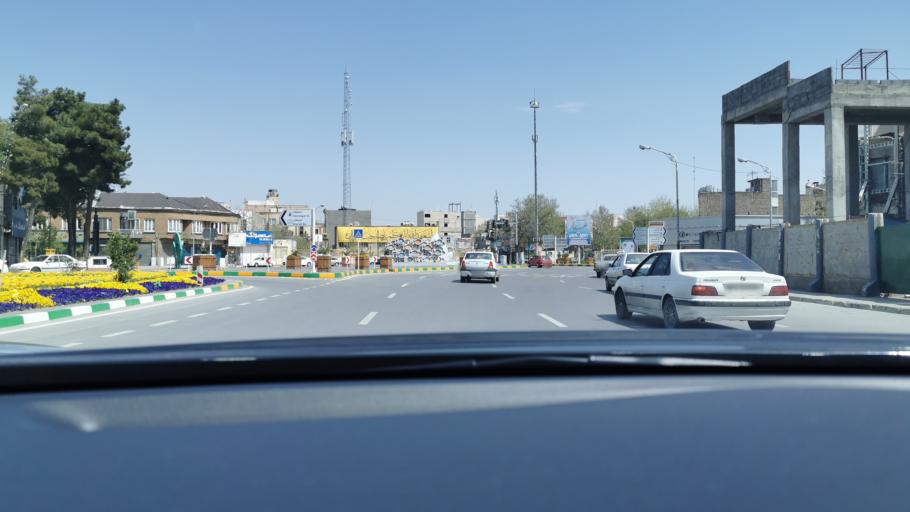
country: IR
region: Razavi Khorasan
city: Mashhad
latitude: 36.2951
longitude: 59.5985
